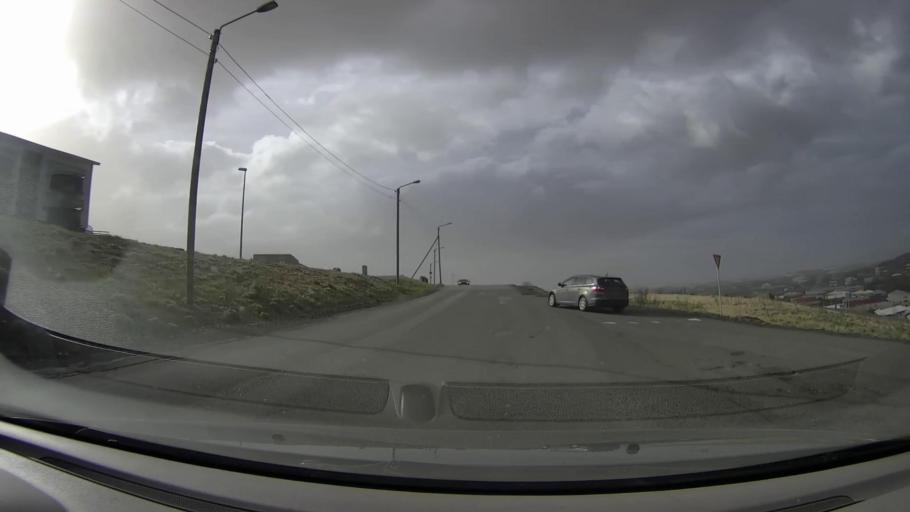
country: IS
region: Capital Region
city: Hafnarfjoerdur
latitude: 64.0580
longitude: -21.9345
